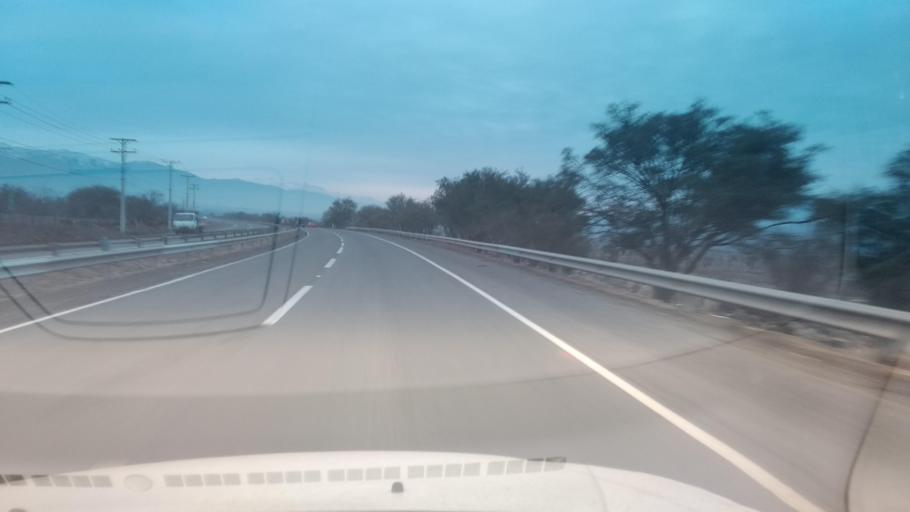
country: CL
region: Santiago Metropolitan
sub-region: Provincia de Chacabuco
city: Chicureo Abajo
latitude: -33.1083
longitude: -70.6893
